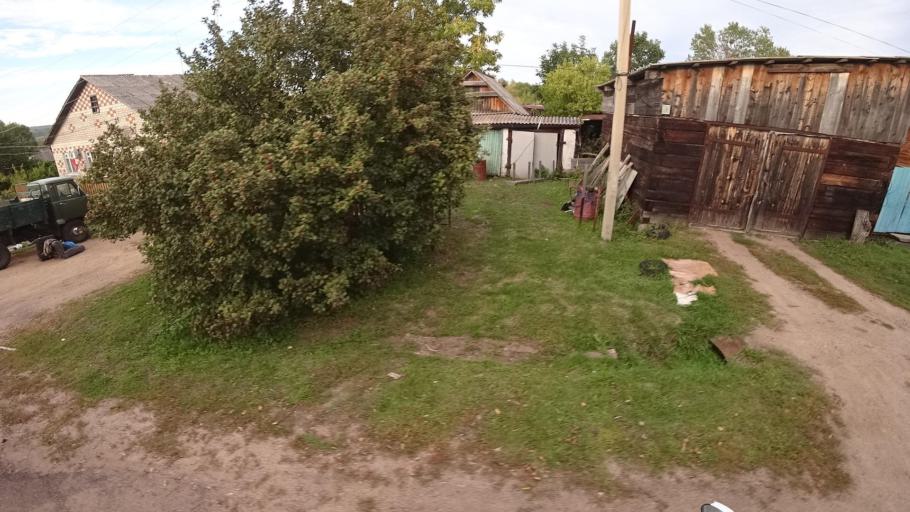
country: RU
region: Primorskiy
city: Yakovlevka
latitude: 44.4122
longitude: 133.4496
